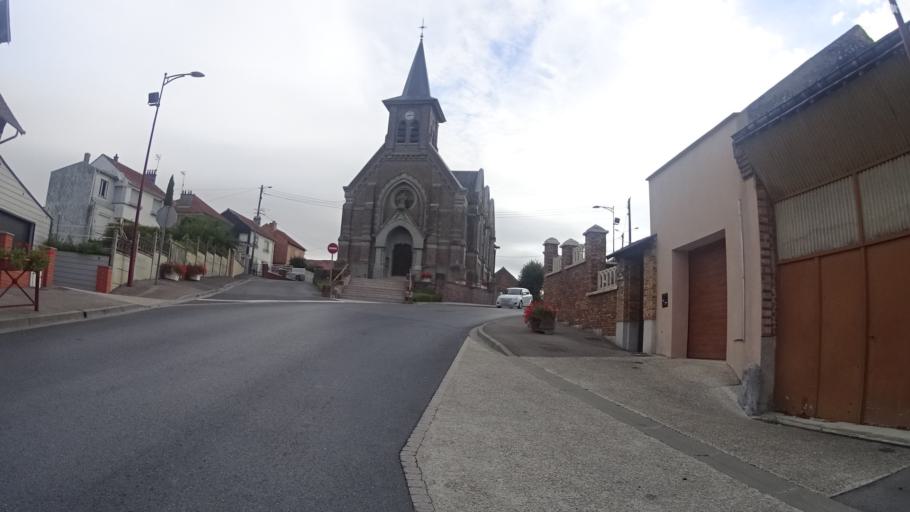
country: FR
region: Picardie
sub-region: Departement de l'Aisne
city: Origny-Sainte-Benoite
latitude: 49.8314
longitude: 3.4688
